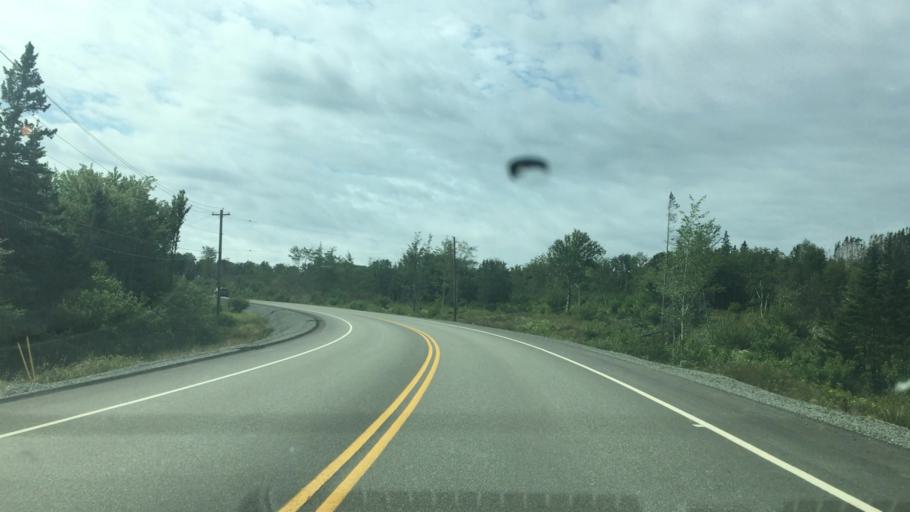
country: CA
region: Nova Scotia
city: Princeville
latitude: 45.6651
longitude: -60.8127
